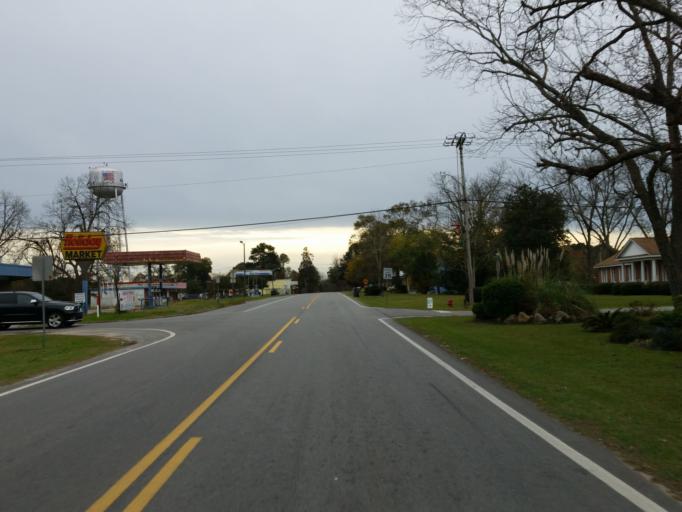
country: US
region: Georgia
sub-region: Crisp County
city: Cordele
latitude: 31.8341
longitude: -83.7411
